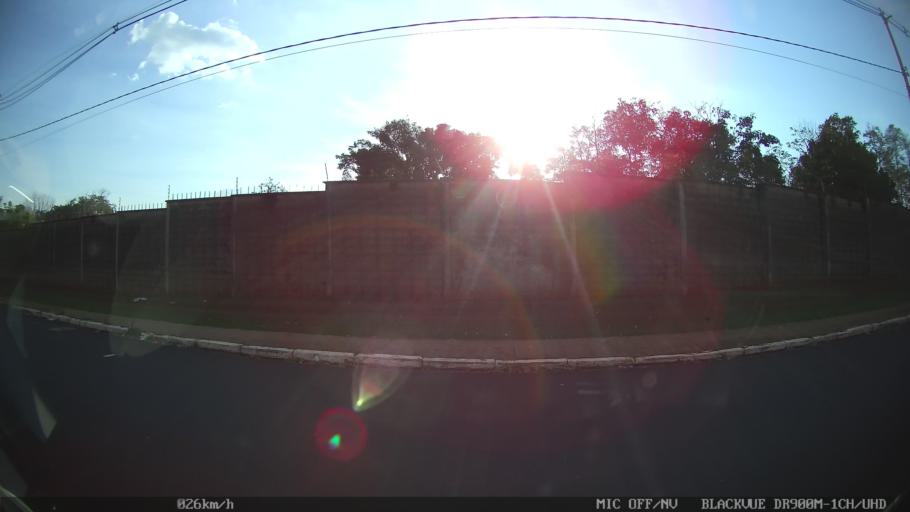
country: BR
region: Sao Paulo
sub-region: Ribeirao Preto
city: Ribeirao Preto
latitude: -21.1647
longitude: -47.8446
